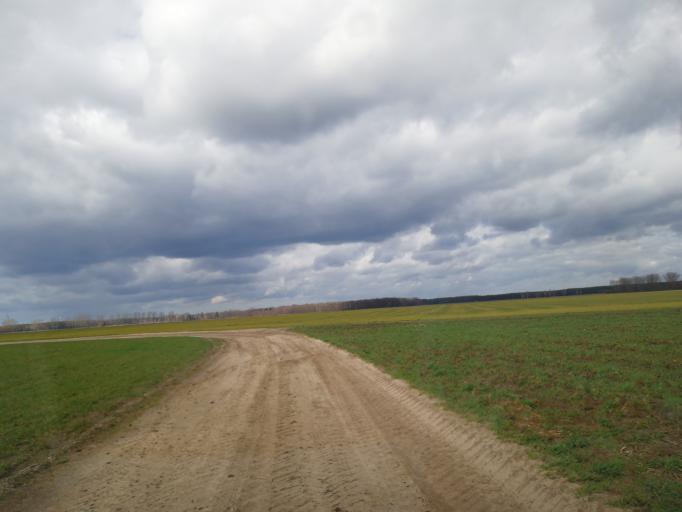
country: DE
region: Brandenburg
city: Schonewalde
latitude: 51.6841
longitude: 13.5554
